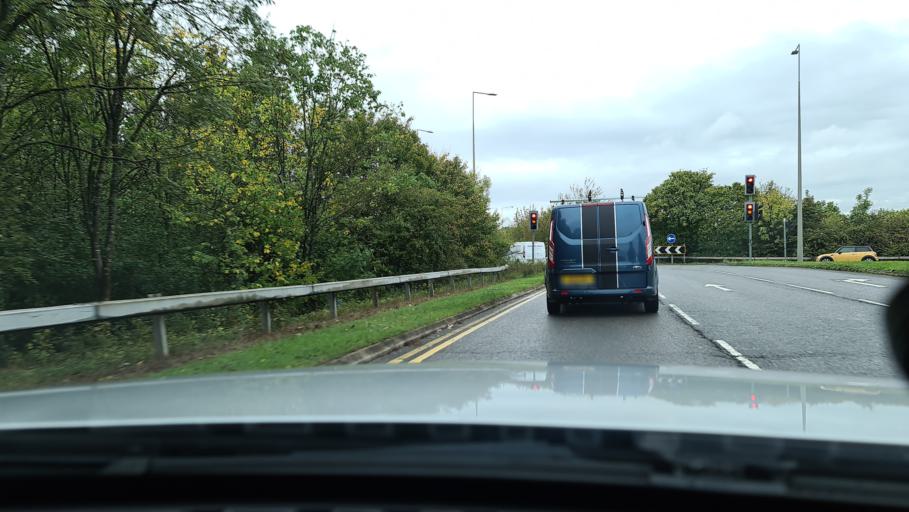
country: GB
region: England
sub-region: Buckinghamshire
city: Bletchley
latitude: 52.0106
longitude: -0.7392
